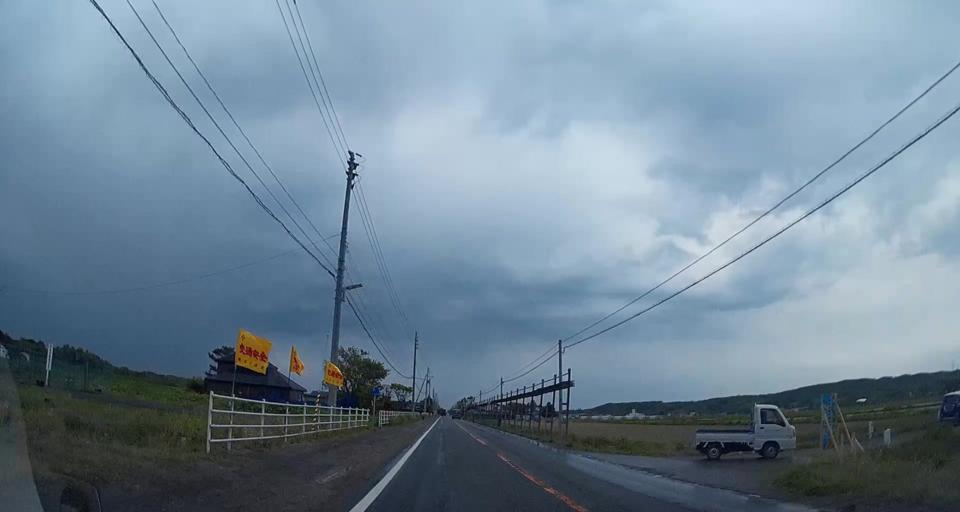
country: JP
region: Hokkaido
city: Chitose
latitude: 42.7316
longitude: 141.8871
